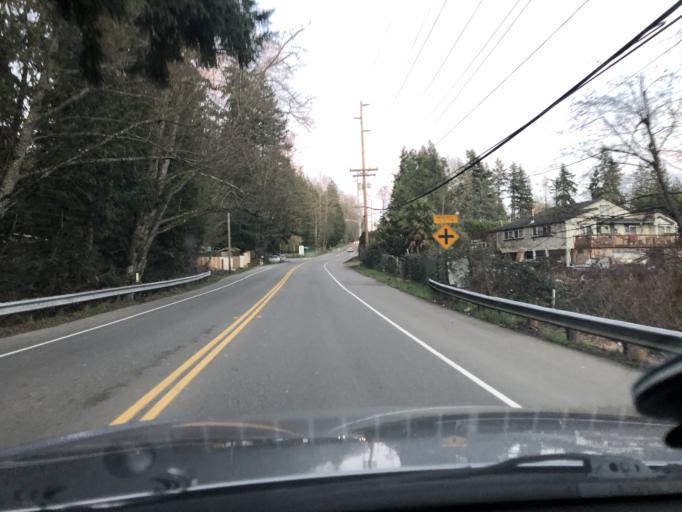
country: US
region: Washington
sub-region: King County
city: Lakeland North
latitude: 47.3144
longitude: -122.2795
